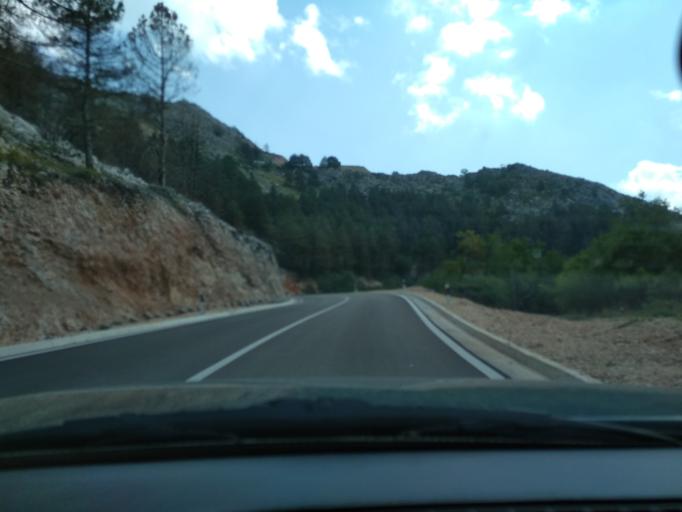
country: ME
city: Dobrota
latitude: 42.4374
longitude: 18.8394
